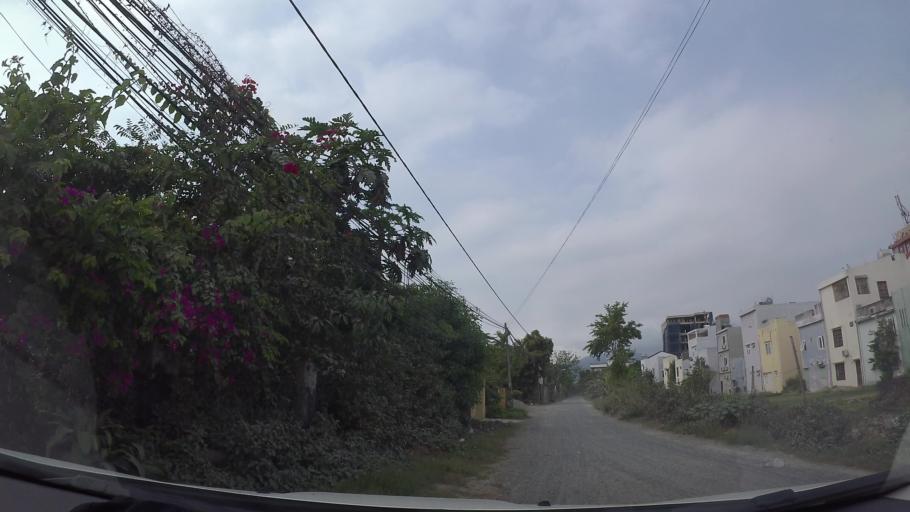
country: VN
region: Da Nang
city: Son Tra
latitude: 16.0754
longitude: 108.2397
